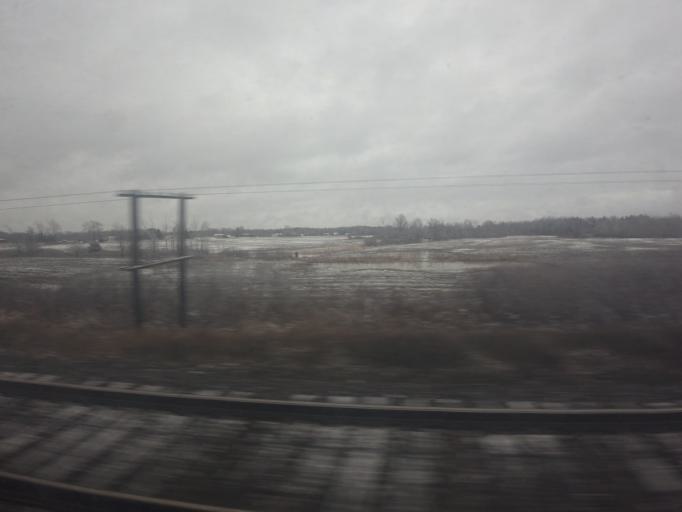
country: US
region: New York
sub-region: Jefferson County
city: Alexandria Bay
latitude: 44.3996
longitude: -76.0242
